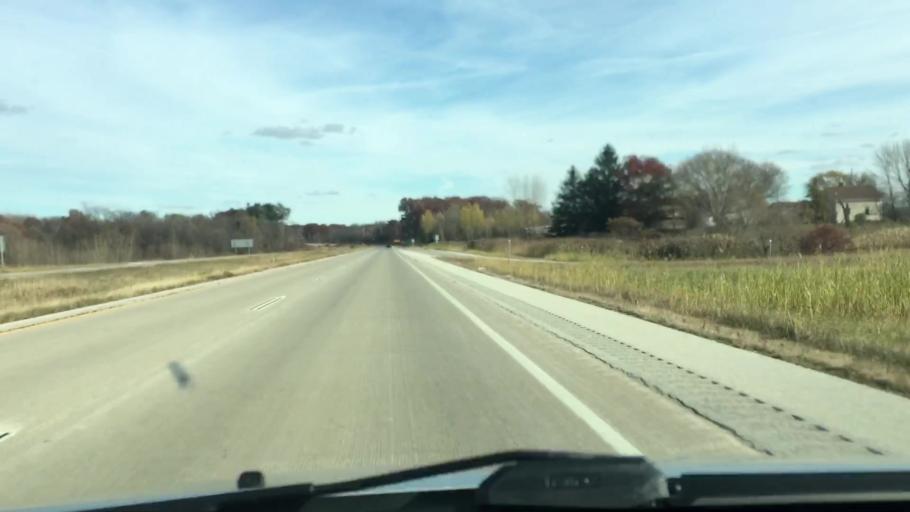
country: US
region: Wisconsin
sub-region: Kewaunee County
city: Luxemburg
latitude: 44.6337
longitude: -87.7725
